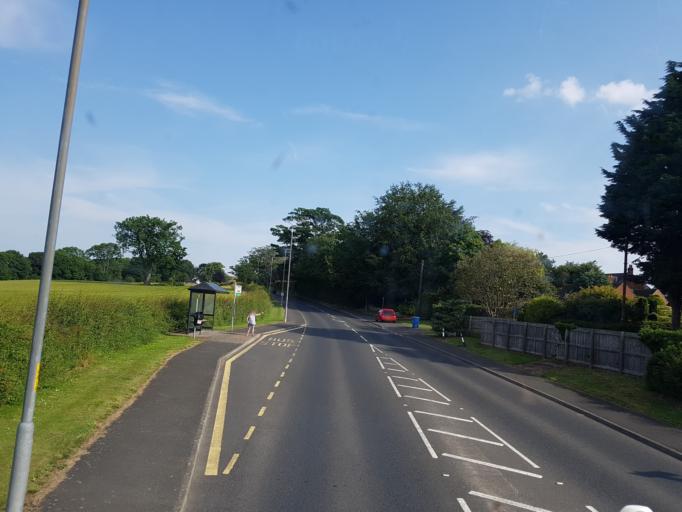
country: GB
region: England
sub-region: Northumberland
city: Alnmouth
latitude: 55.3988
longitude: -1.6352
